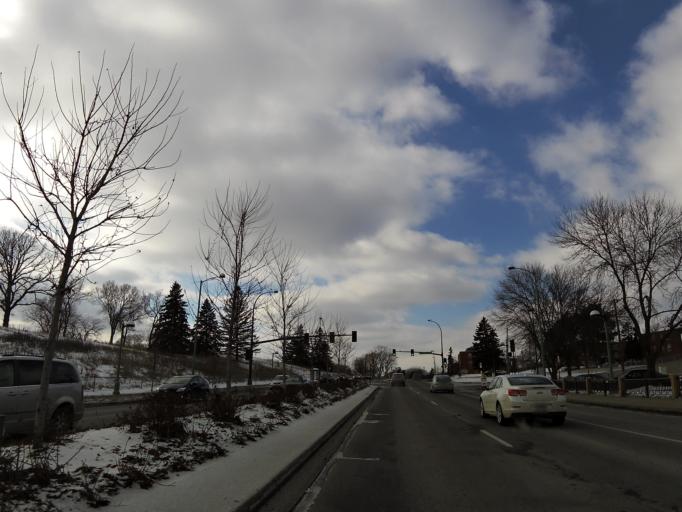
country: US
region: Minnesota
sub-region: Hennepin County
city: Saint Louis Park
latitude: 44.9271
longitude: -93.3640
